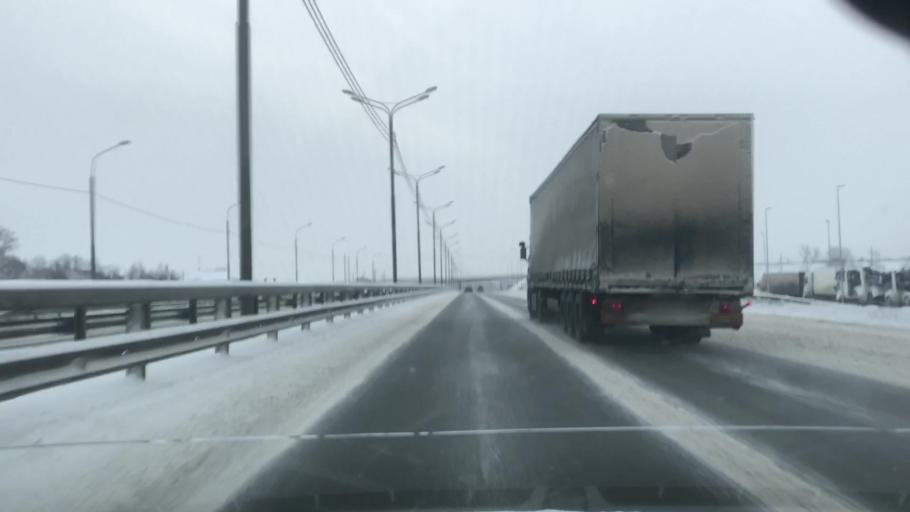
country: RU
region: Moskovskaya
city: Barybino
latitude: 55.2863
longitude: 37.8557
